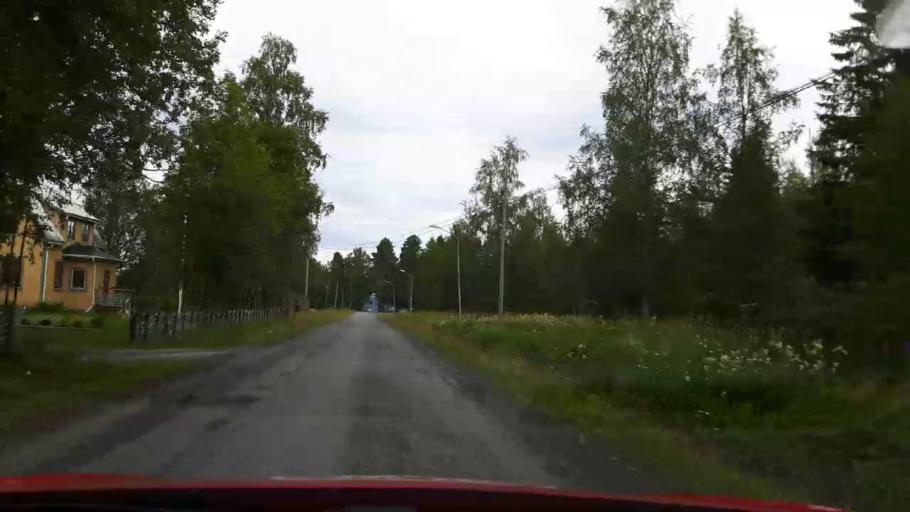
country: SE
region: Jaemtland
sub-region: Stroemsunds Kommun
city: Stroemsund
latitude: 63.5199
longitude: 15.3509
